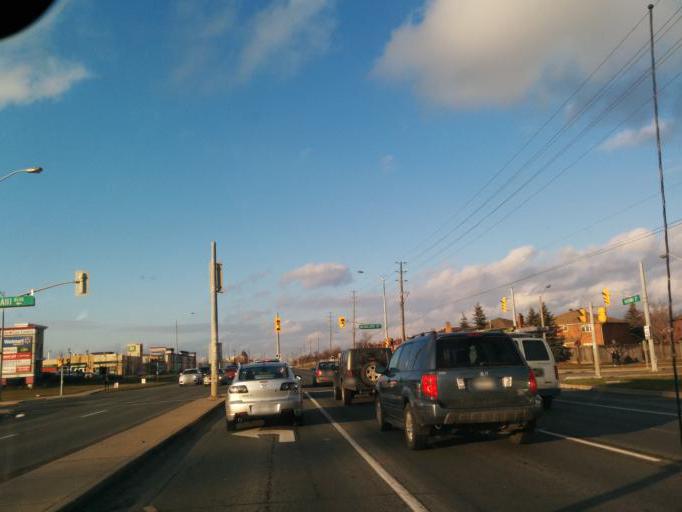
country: CA
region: Ontario
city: Vaughan
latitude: 43.7837
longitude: -79.6241
